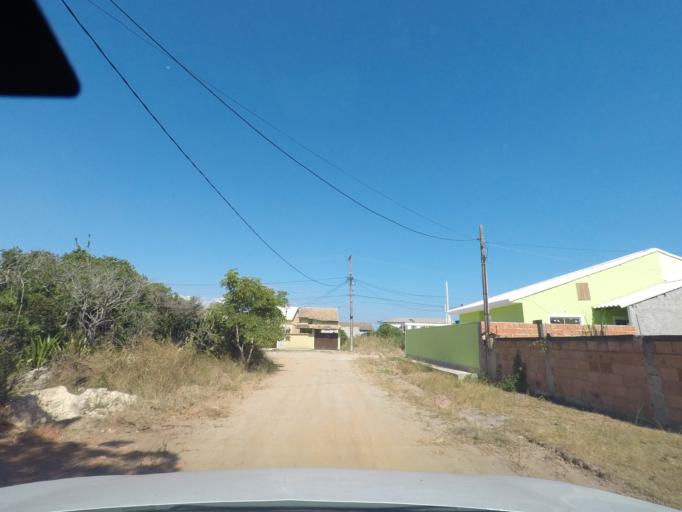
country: BR
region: Rio de Janeiro
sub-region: Marica
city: Marica
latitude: -22.9680
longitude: -42.9059
